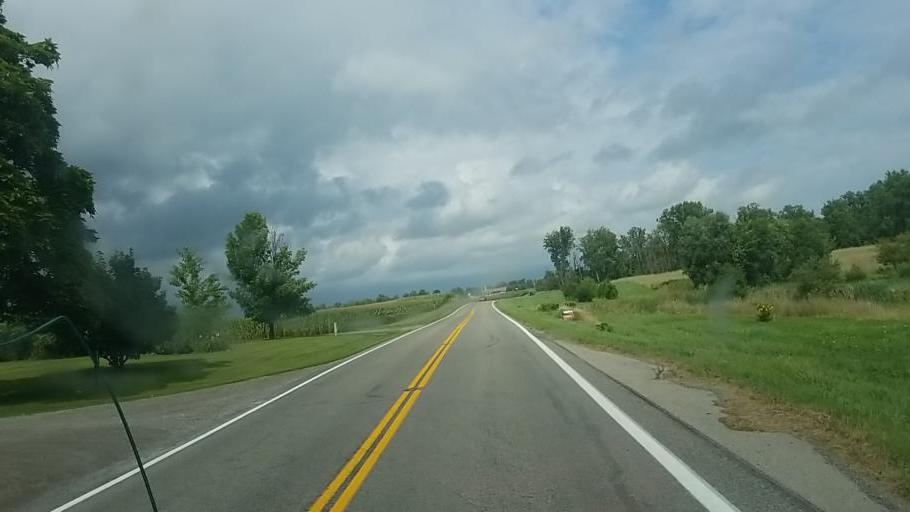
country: US
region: Ohio
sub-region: Champaign County
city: North Lewisburg
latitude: 40.2845
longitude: -83.5907
